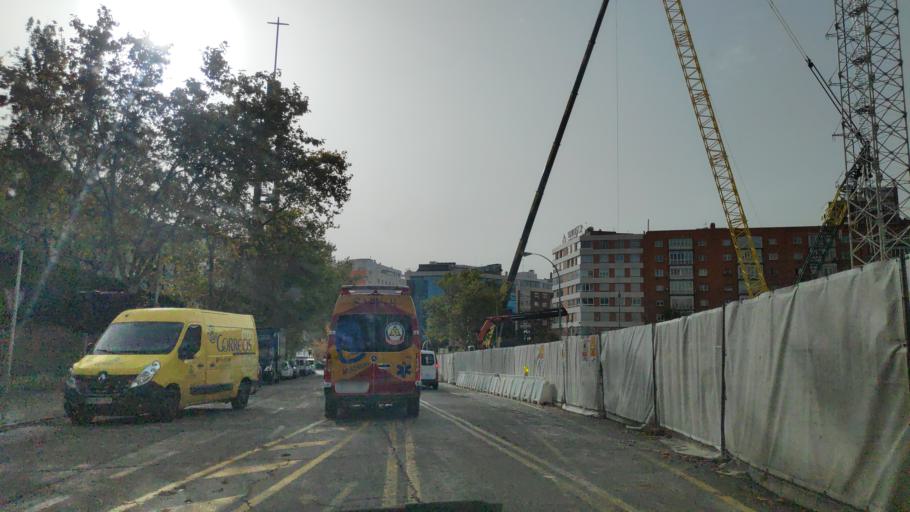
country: ES
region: Madrid
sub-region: Provincia de Madrid
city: Chamartin
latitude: 40.4531
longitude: -3.6866
